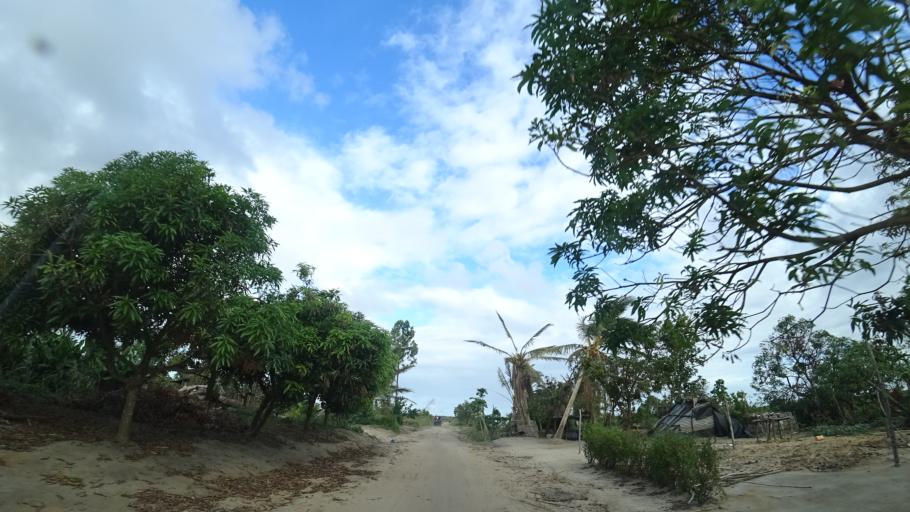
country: MZ
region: Sofala
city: Beira
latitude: -19.6577
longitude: 35.0617
